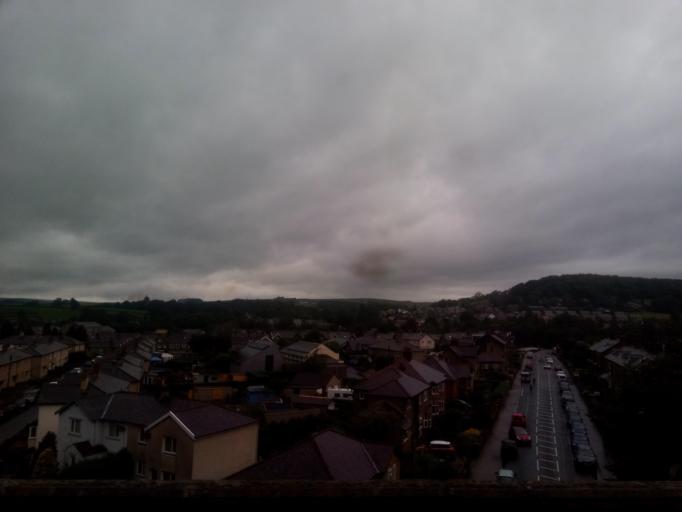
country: GB
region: England
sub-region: North Yorkshire
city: Settle
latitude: 54.0704
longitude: -2.2787
